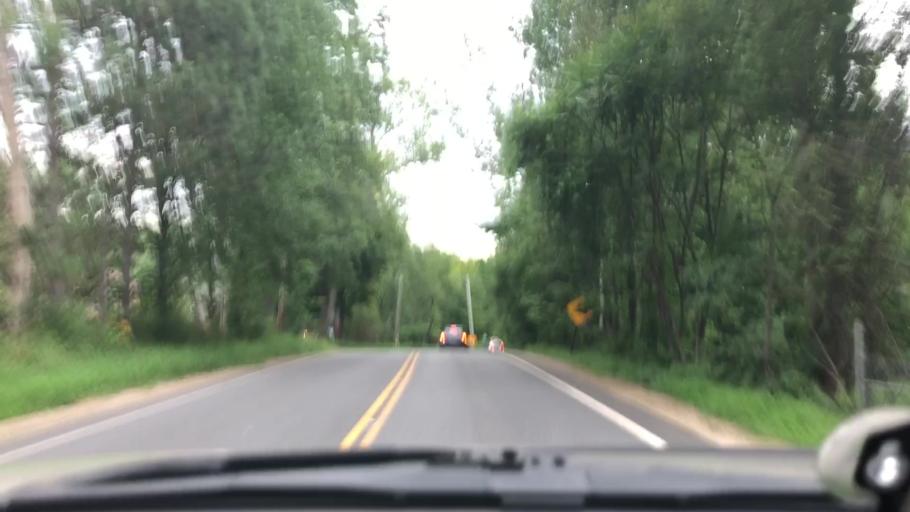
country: US
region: New York
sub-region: Saratoga County
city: Corinth
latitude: 43.2062
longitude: -73.7729
